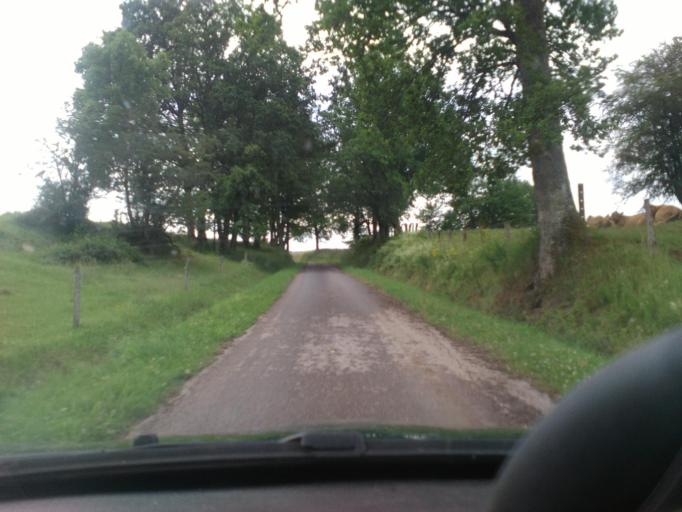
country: FR
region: Lorraine
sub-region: Departement des Vosges
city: Moyenmoutier
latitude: 48.3468
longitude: 6.9399
